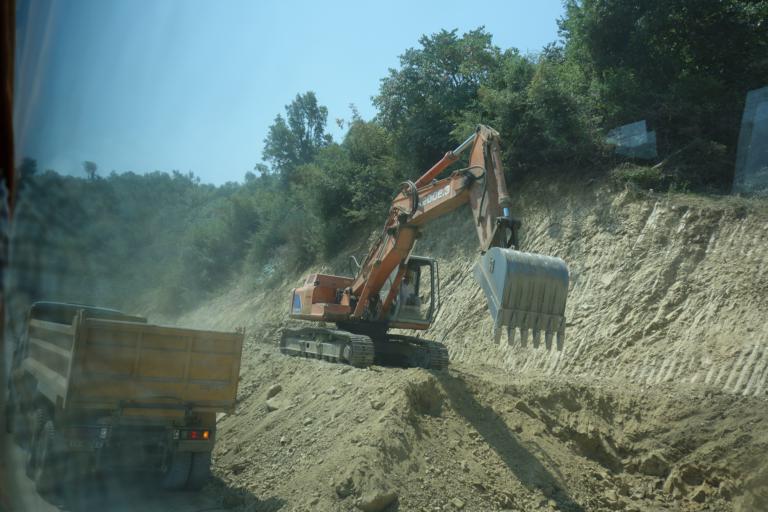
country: AL
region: Gjirokaster
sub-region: Rrethi i Tepelenes
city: Memaliaj
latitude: 40.3453
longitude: 19.9793
